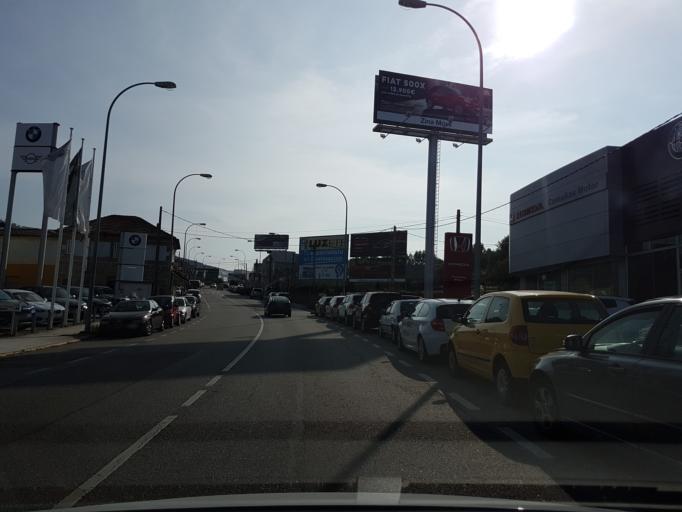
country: ES
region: Galicia
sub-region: Provincia de Pontevedra
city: Vigo
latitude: 42.1982
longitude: -8.7633
